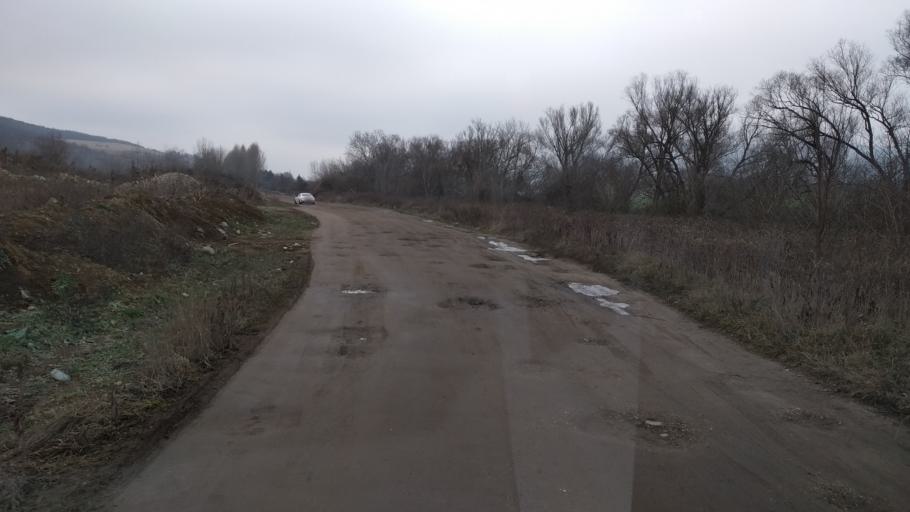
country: HU
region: Pest
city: Pilisborosjeno
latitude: 47.6019
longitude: 18.9681
